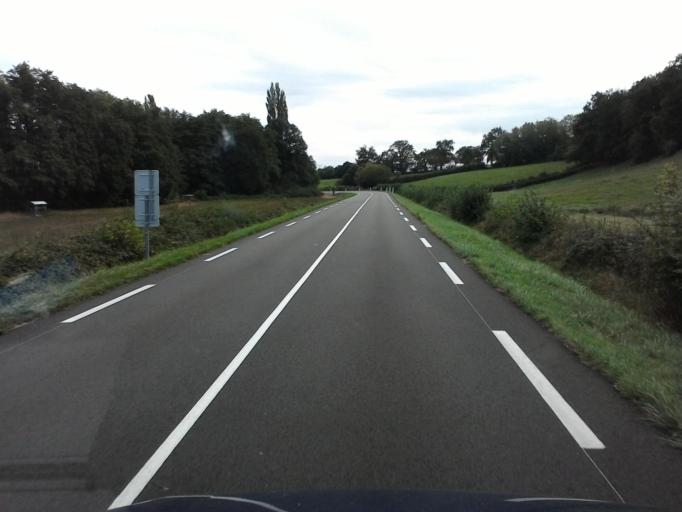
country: FR
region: Bourgogne
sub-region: Departement de Saone-et-Loire
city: Saint-Gengoux-le-National
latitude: 46.5809
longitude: 4.5224
